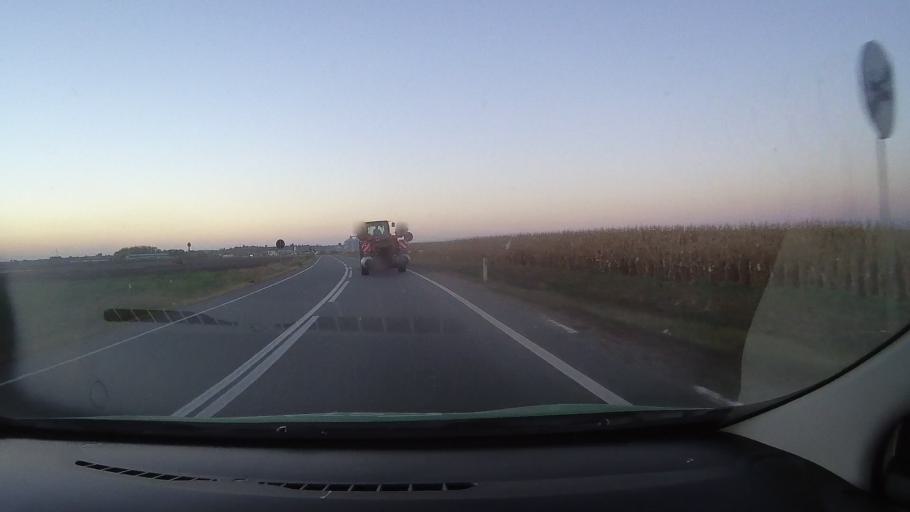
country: RO
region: Bihor
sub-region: Comuna Tarcea
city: Tarcea
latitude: 47.4495
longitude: 22.1852
